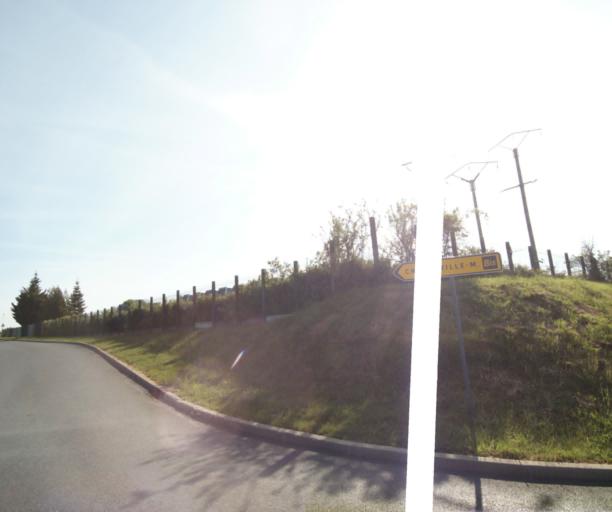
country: FR
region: Champagne-Ardenne
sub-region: Departement des Ardennes
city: La Francheville
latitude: 49.7364
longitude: 4.7098
